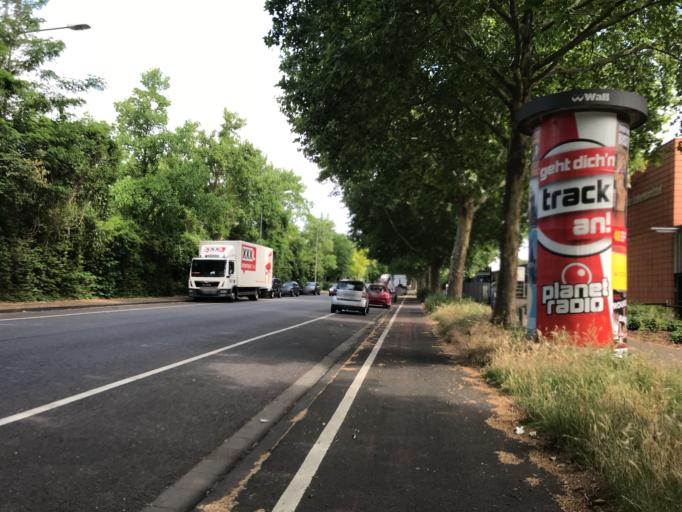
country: DE
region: Rheinland-Pfalz
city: Budenheim
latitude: 50.0445
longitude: 8.2048
